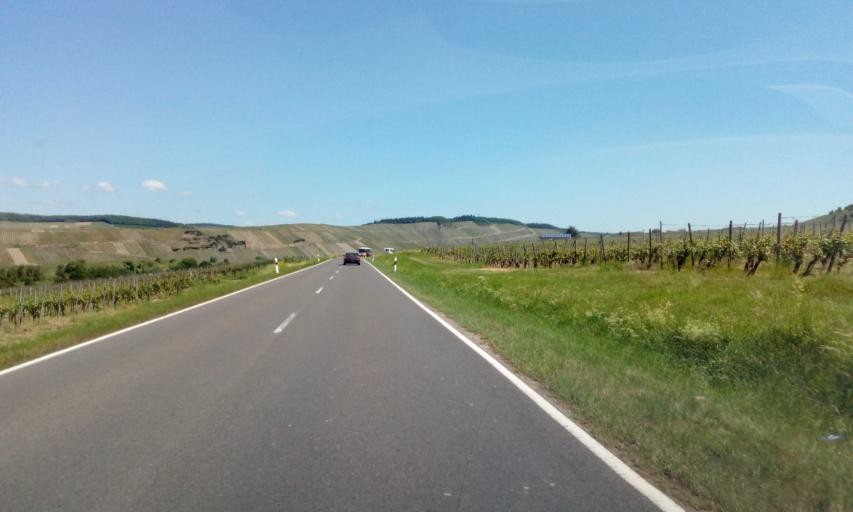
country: DE
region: Rheinland-Pfalz
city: Kesten
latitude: 49.8954
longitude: 6.9631
